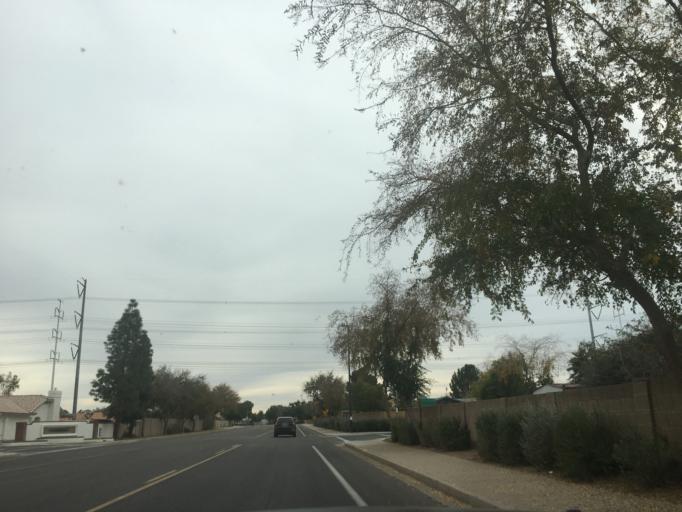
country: US
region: Arizona
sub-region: Maricopa County
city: Gilbert
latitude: 33.3588
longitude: -111.7820
